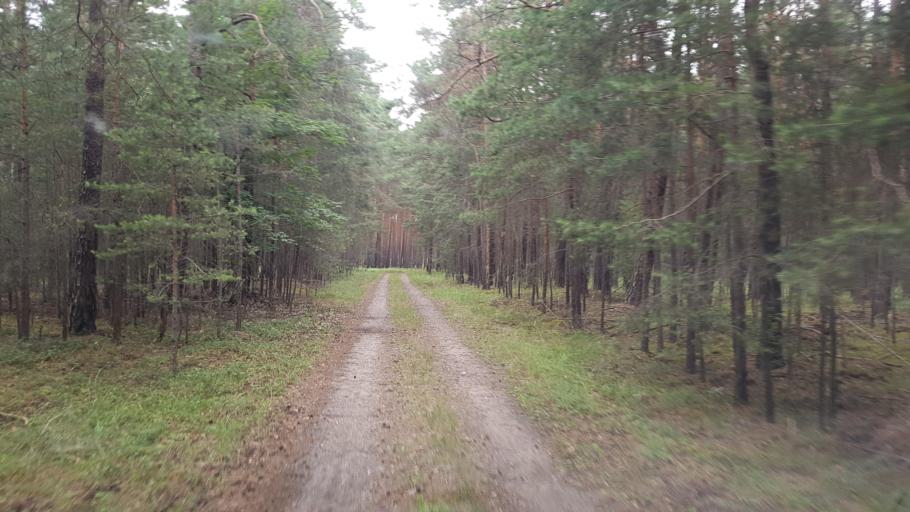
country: DE
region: Brandenburg
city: Grossraschen
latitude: 51.5993
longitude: 14.0369
